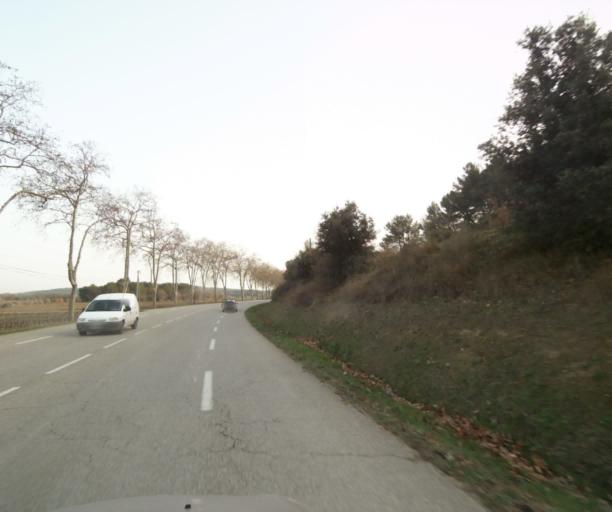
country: FR
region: Provence-Alpes-Cote d'Azur
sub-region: Departement des Bouches-du-Rhone
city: Rognes
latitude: 43.6522
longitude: 5.3571
